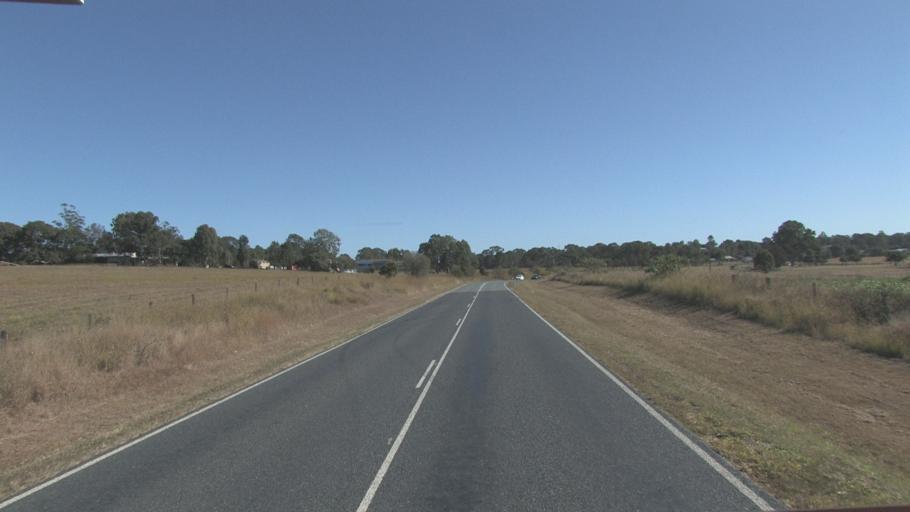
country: AU
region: Queensland
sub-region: Logan
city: Chambers Flat
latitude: -27.7674
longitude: 153.0995
